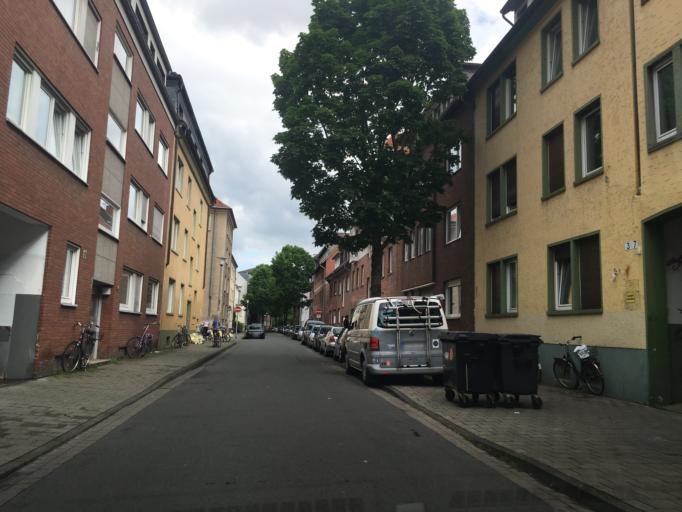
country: DE
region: North Rhine-Westphalia
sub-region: Regierungsbezirk Munster
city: Muenster
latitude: 51.9589
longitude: 7.6434
